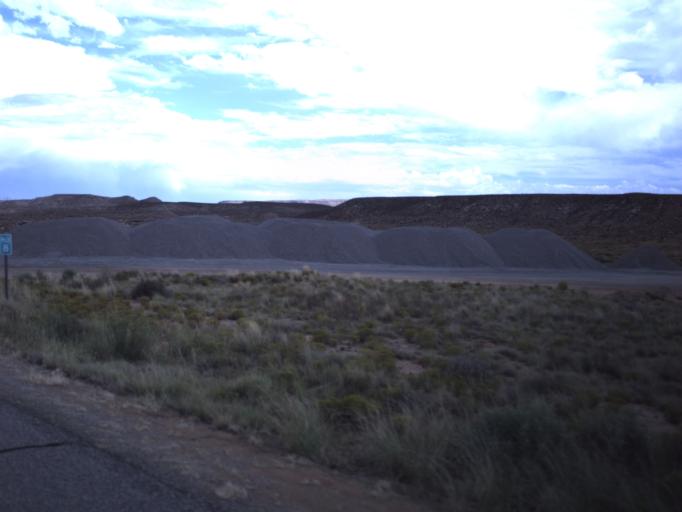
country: US
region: Utah
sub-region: San Juan County
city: Blanding
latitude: 37.2915
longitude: -109.4144
